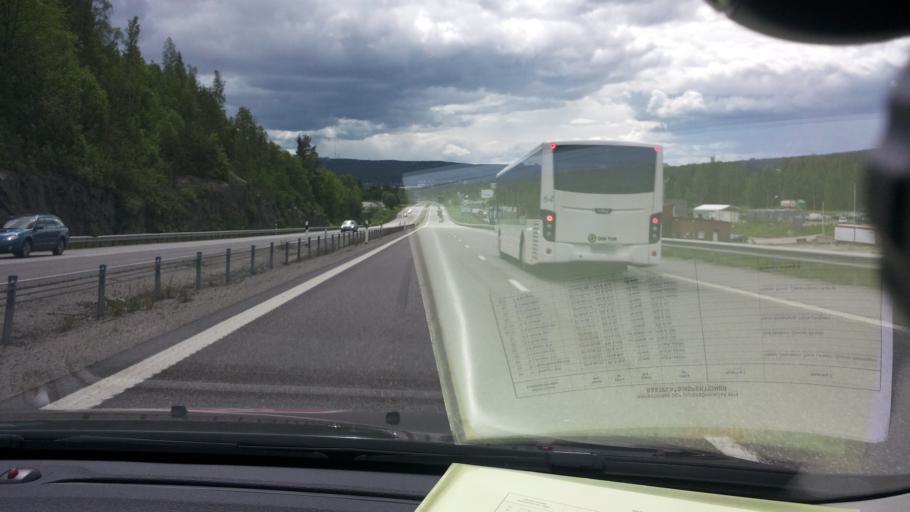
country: SE
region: Vaesternorrland
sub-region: Sundsvalls Kommun
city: Johannedal
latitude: 62.4216
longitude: 17.3483
